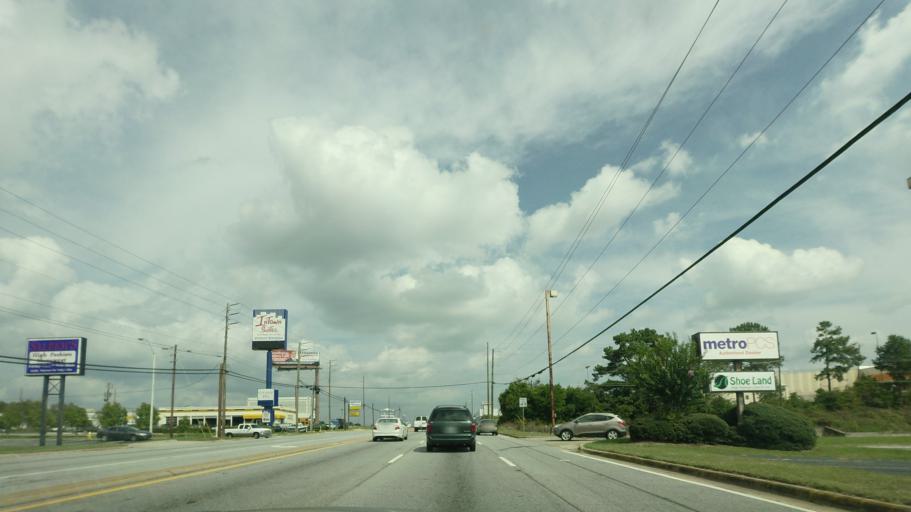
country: US
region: Georgia
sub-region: Bibb County
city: Macon
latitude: 32.8145
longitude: -83.6675
